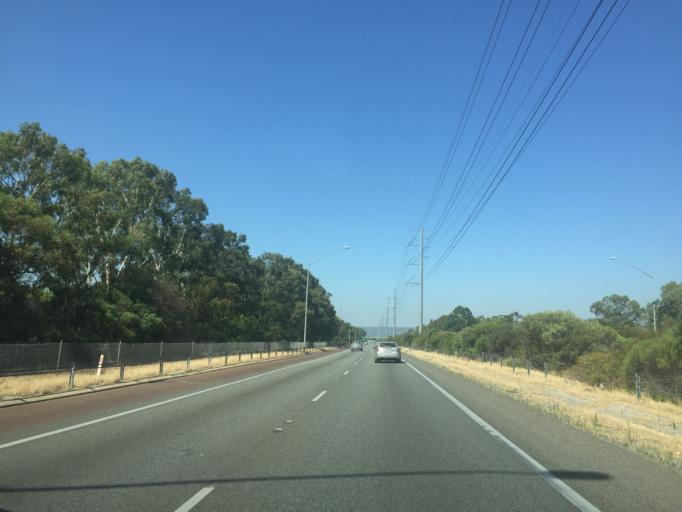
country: AU
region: Western Australia
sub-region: Gosnells
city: Langford
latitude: -32.0501
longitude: 115.9393
